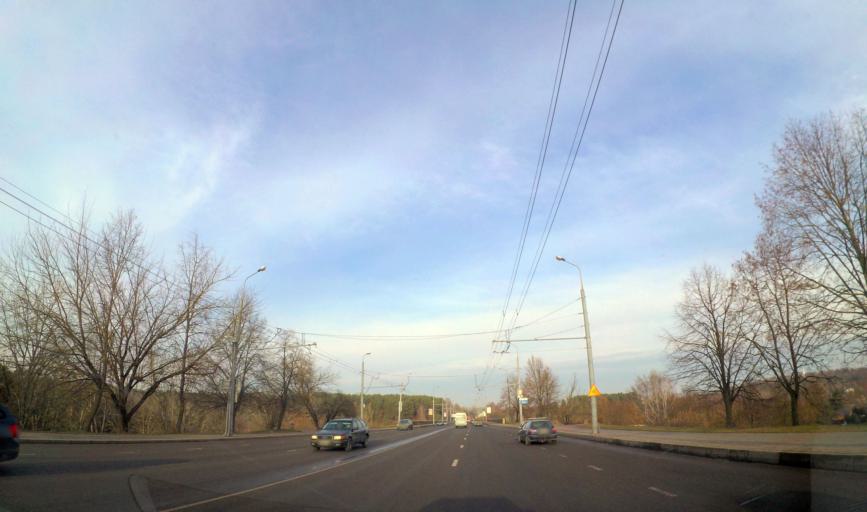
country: BY
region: Grodnenskaya
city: Hrodna
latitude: 53.6771
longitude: 23.8055
